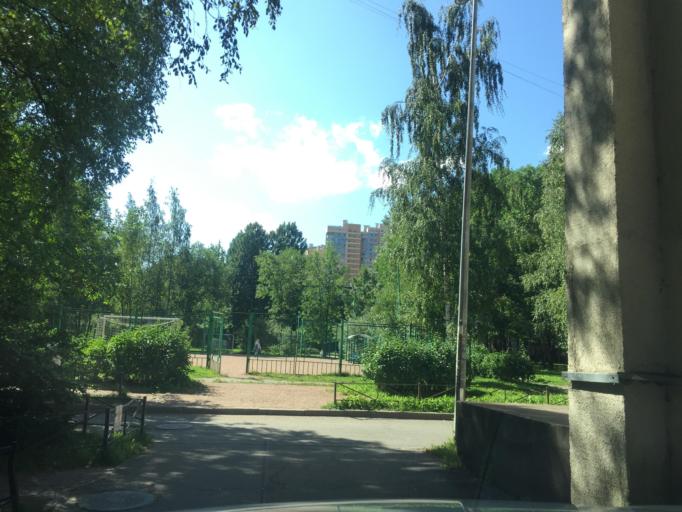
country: RU
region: Leningrad
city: Akademicheskoe
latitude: 60.0076
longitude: 30.4076
